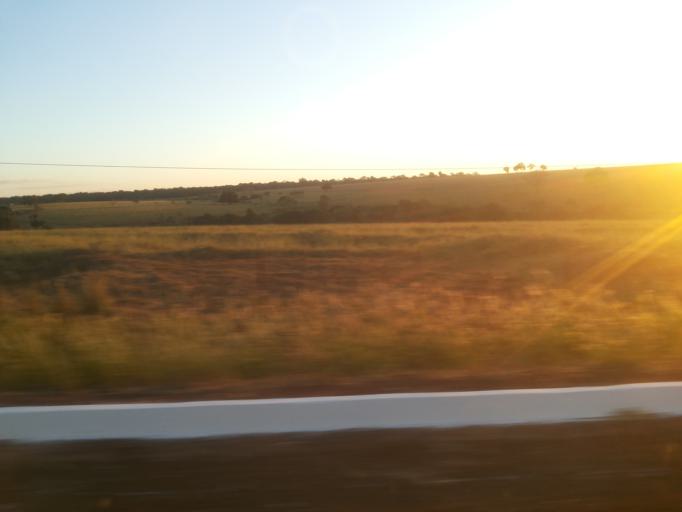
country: BR
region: Minas Gerais
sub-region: Capinopolis
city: Capinopolis
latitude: -18.7180
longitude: -49.5569
